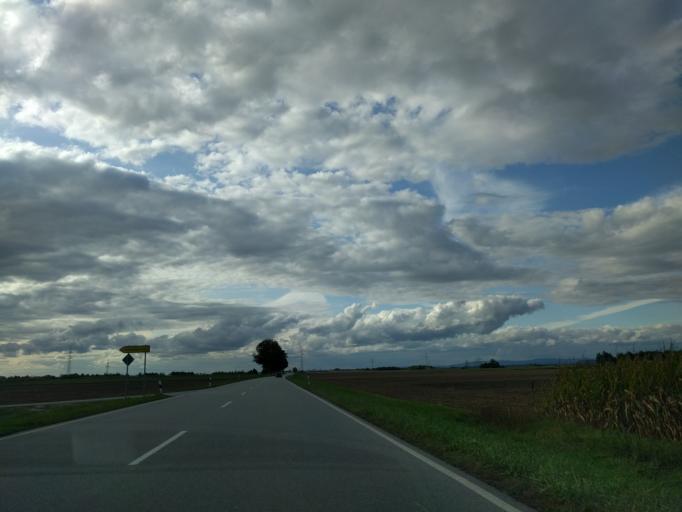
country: DE
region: Bavaria
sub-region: Lower Bavaria
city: Stephansposching
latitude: 48.8083
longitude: 12.7803
